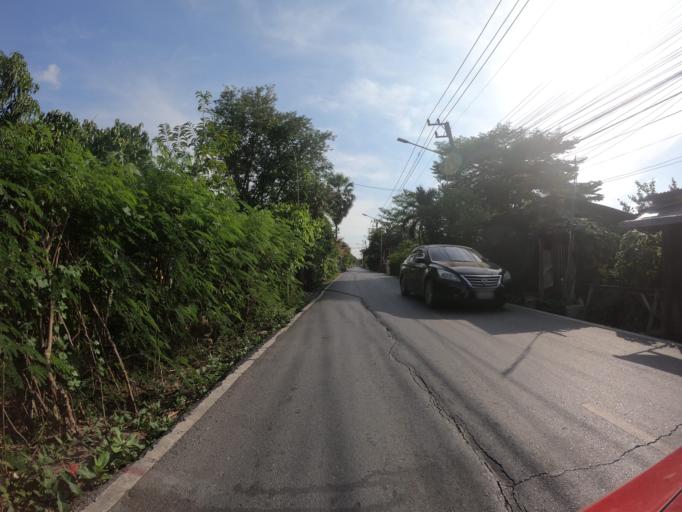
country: TH
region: Pathum Thani
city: Thanyaburi
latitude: 14.0156
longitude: 100.7325
